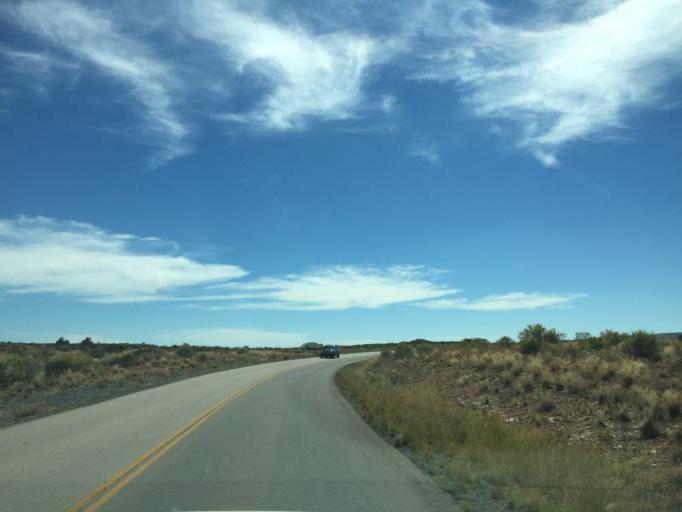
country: US
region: Arizona
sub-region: Mohave County
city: Meadview
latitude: 35.9698
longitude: -113.8189
